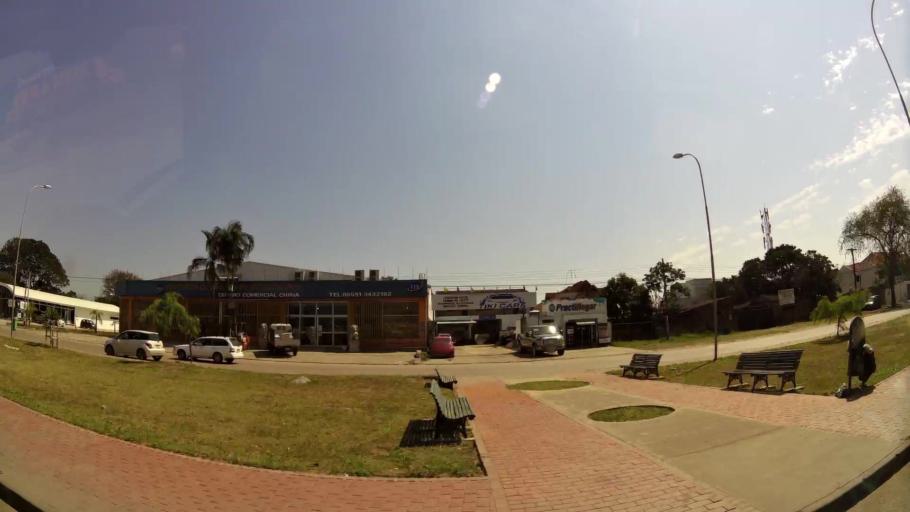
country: BO
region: Santa Cruz
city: Santa Cruz de la Sierra
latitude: -17.7493
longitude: -63.1629
